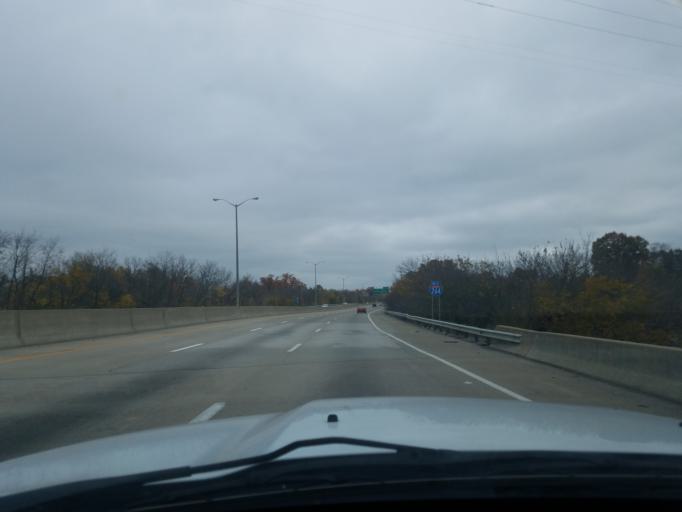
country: US
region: Indiana
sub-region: Floyd County
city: New Albany
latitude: 38.2435
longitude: -85.8134
